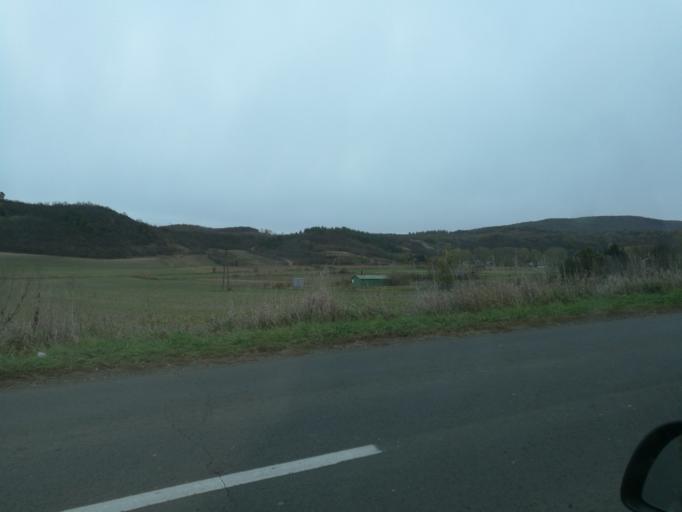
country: HU
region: Nograd
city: Rimoc
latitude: 48.0412
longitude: 19.5641
